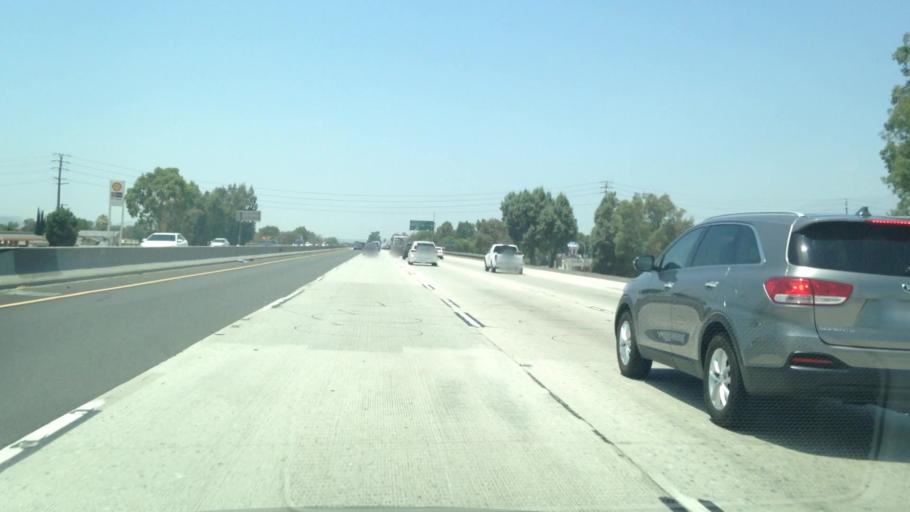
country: US
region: California
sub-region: San Bernardino County
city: Loma Linda
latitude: 34.0670
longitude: -117.2410
